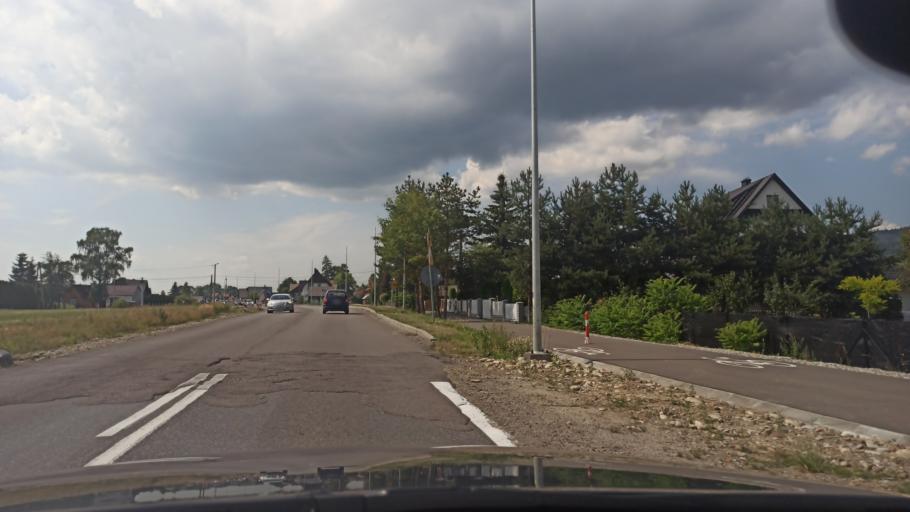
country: PL
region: Lesser Poland Voivodeship
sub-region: Powiat nowotarski
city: Lopuszna
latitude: 49.4731
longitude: 20.1782
